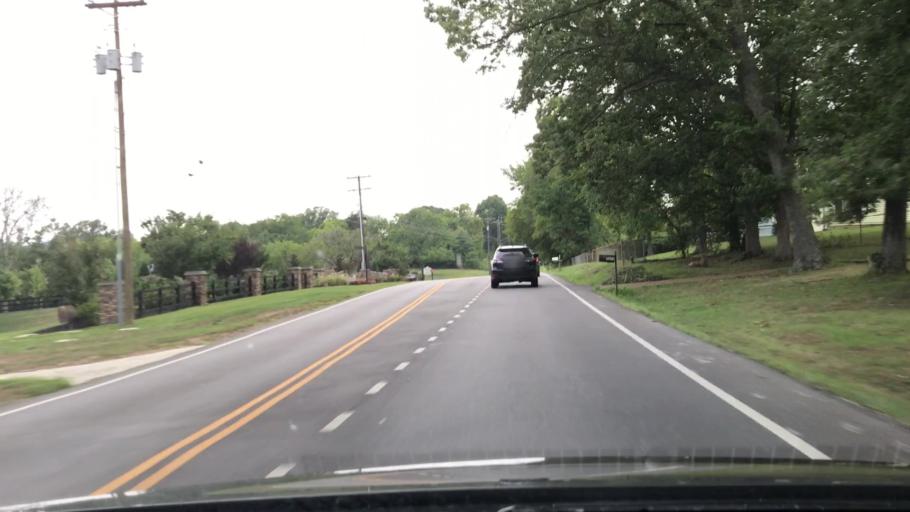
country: US
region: Tennessee
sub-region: Williamson County
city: Nolensville
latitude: 35.9373
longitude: -86.6916
